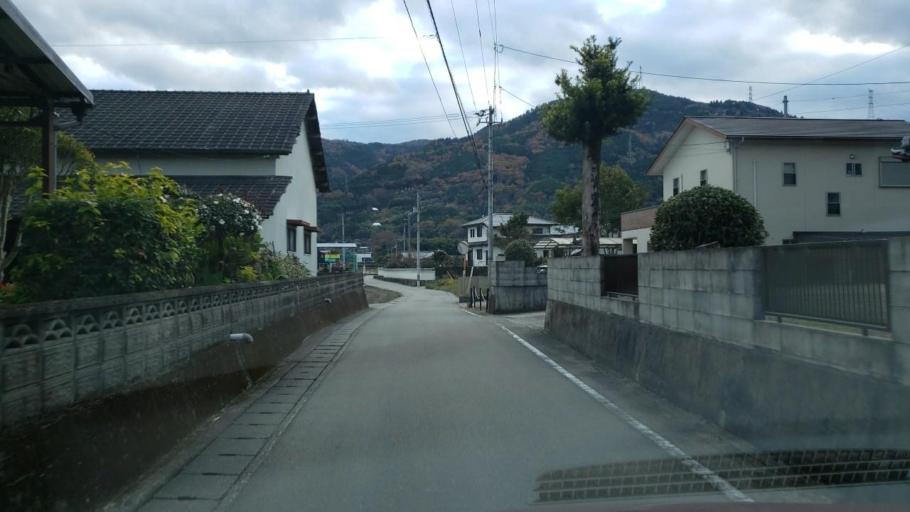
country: JP
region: Tokushima
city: Wakimachi
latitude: 34.0607
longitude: 134.1436
